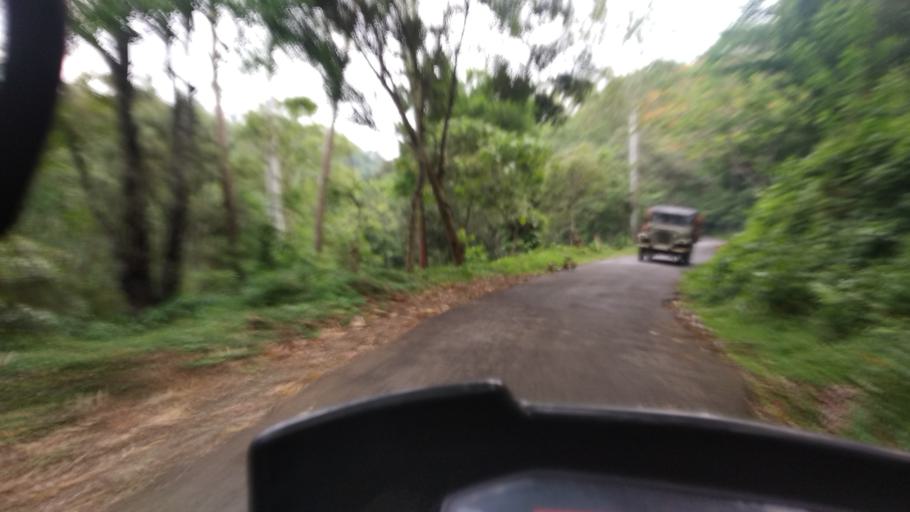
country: IN
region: Tamil Nadu
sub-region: Theni
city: Gudalur
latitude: 9.5516
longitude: 77.0615
